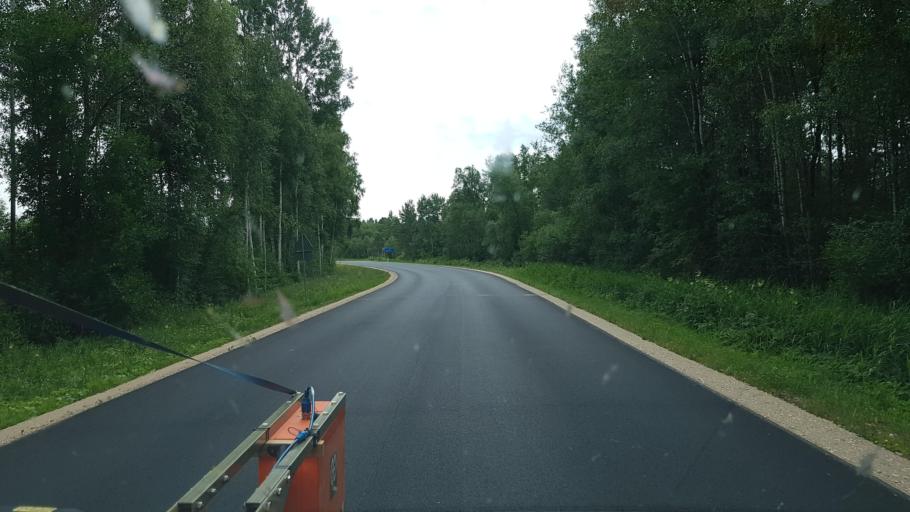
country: EE
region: Paernumaa
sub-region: Audru vald
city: Audru
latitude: 58.6236
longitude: 24.2635
